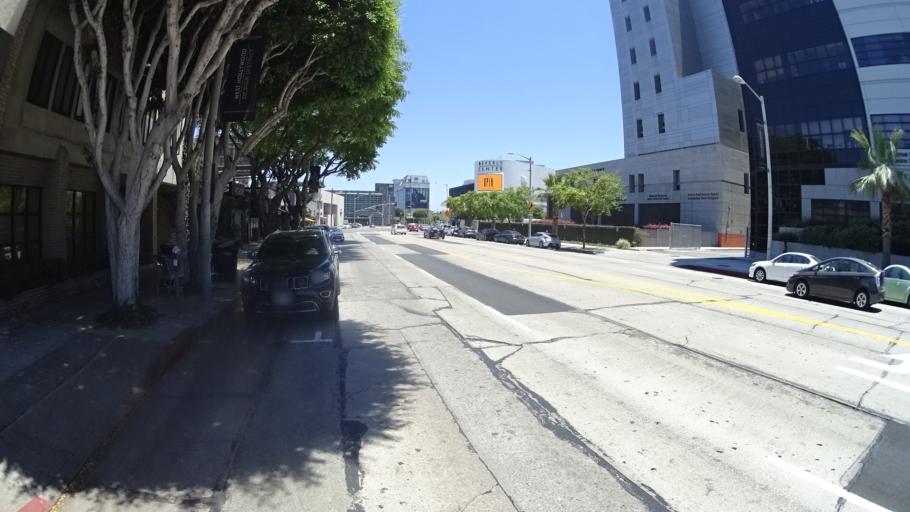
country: US
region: California
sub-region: Los Angeles County
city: Beverly Hills
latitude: 34.0766
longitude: -118.3813
